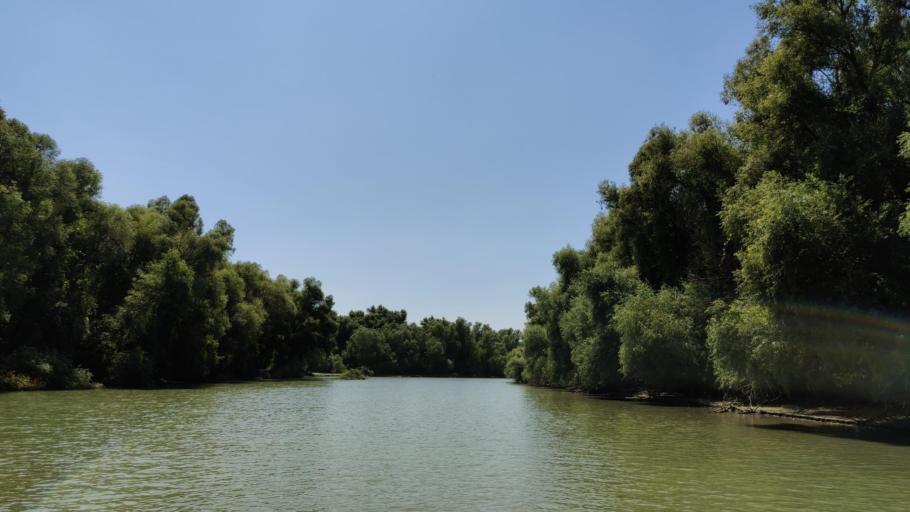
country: RO
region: Tulcea
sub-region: Comuna Pardina
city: Pardina
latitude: 45.2381
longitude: 28.9179
